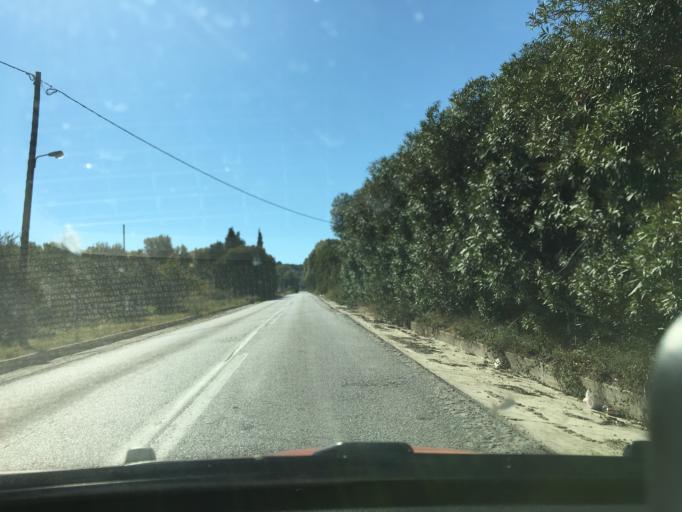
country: GR
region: Central Macedonia
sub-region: Nomos Chalkidikis
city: Ierissos
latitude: 40.3919
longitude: 23.8940
